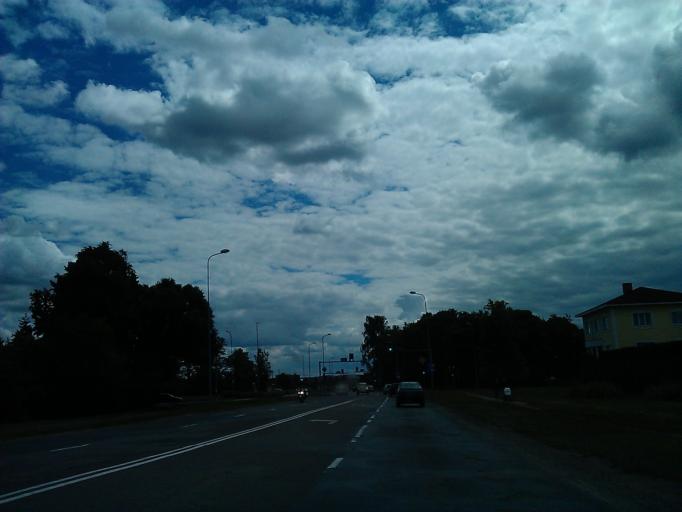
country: LV
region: Jelgava
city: Jelgava
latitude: 56.6429
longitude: 23.6949
